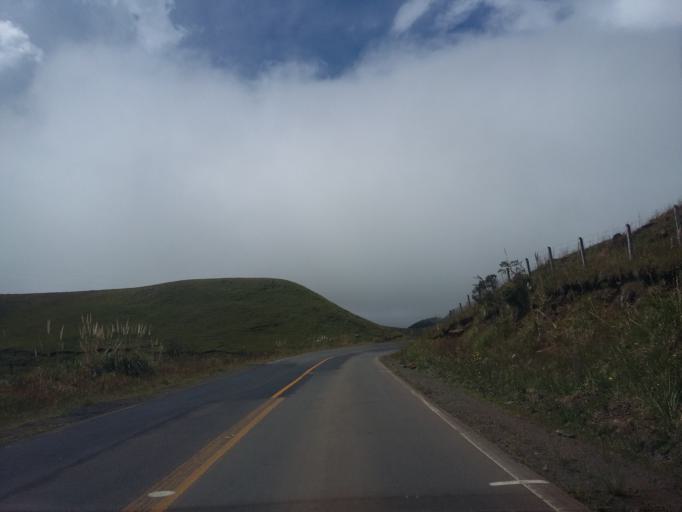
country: BR
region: Santa Catarina
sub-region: Lauro Muller
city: Lauro Muller
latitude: -28.3719
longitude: -49.5651
